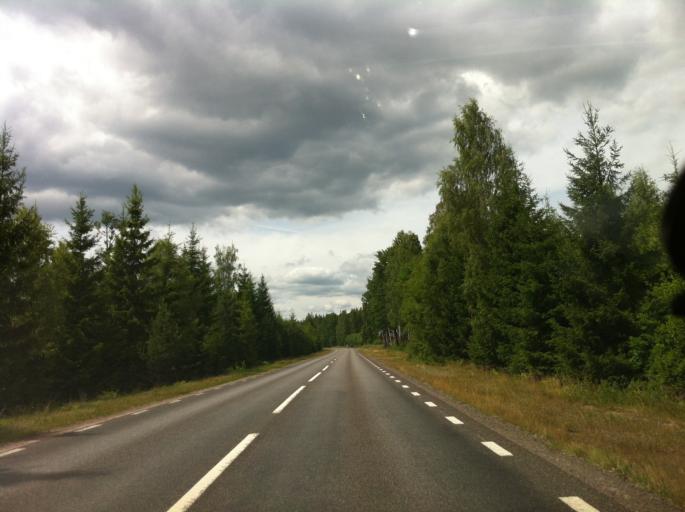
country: SE
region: Kalmar
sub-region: Emmaboda Kommun
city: Emmaboda
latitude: 56.6304
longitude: 15.5086
